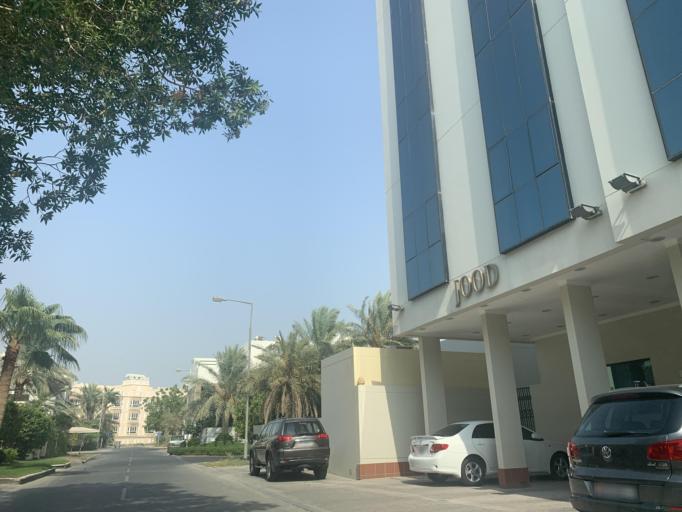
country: BH
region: Manama
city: Jidd Hafs
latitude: 26.2052
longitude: 50.4941
